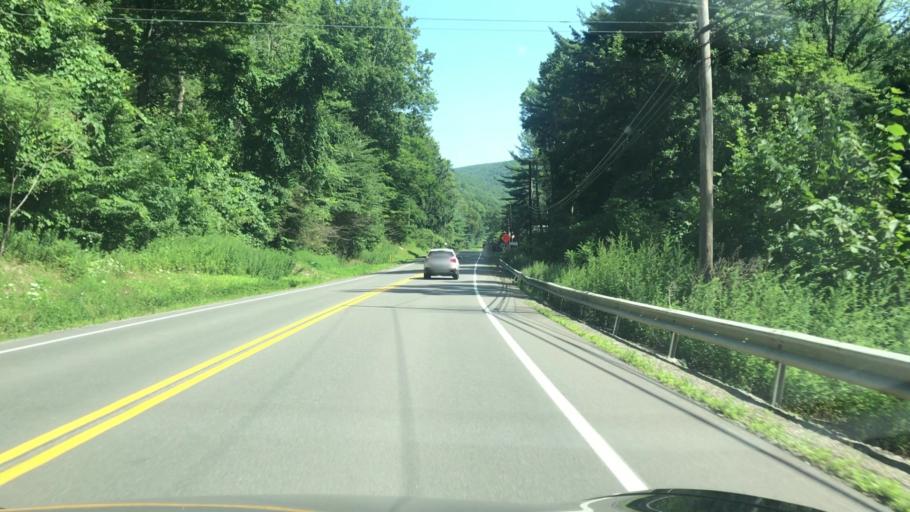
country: US
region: Pennsylvania
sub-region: Lycoming County
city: Kenmar
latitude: 41.4718
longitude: -76.9810
